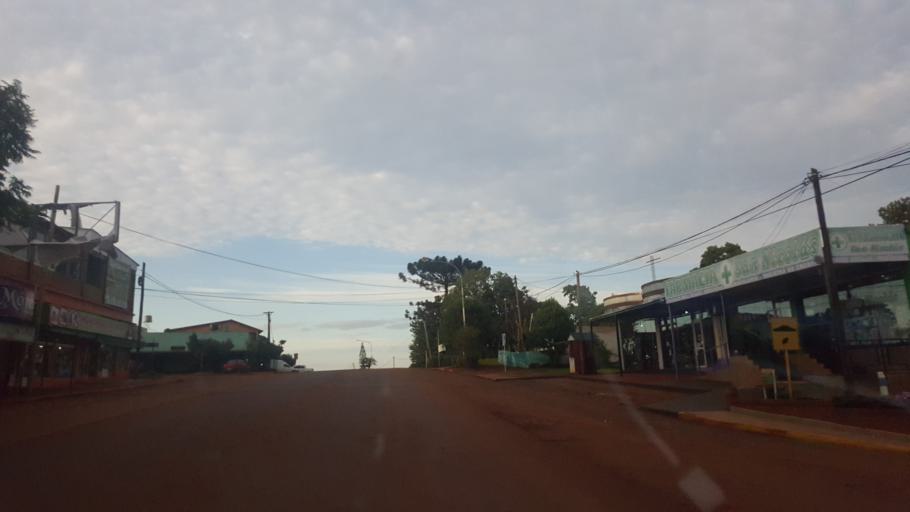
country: AR
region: Misiones
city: Dos de Mayo
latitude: -27.0259
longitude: -54.6873
